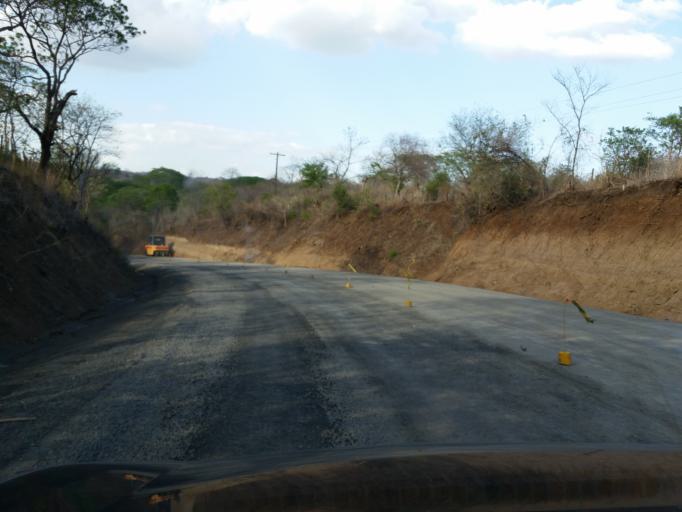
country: NI
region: Managua
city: Carlos Fonseca Amador
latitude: 12.0632
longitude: -86.4514
